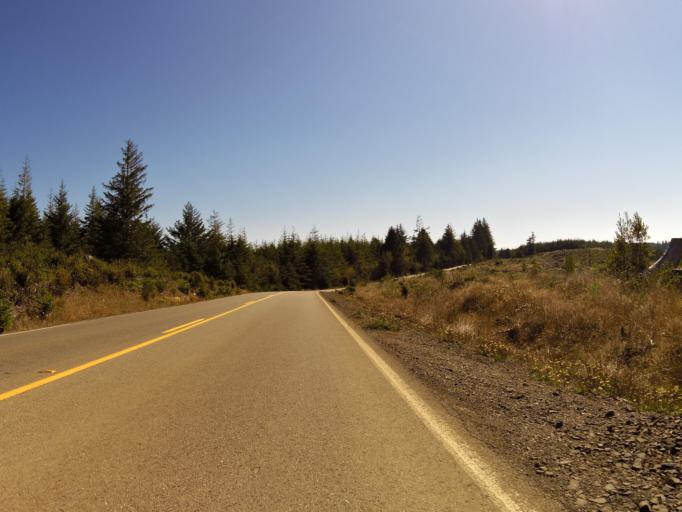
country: US
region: Oregon
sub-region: Coos County
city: Barview
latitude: 43.2563
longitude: -124.3373
